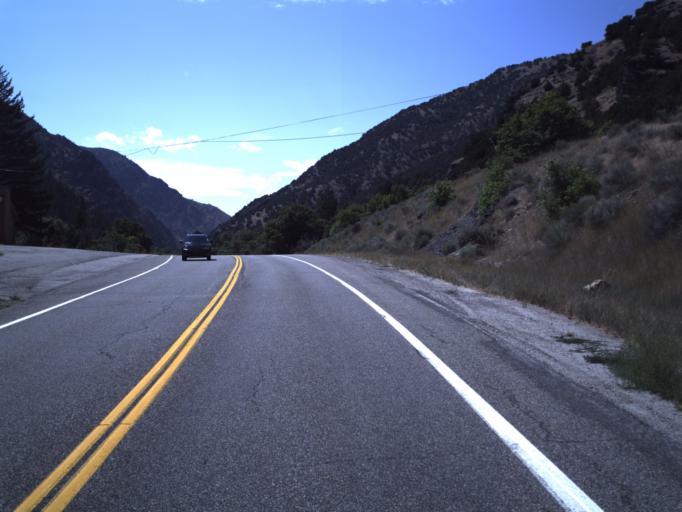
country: US
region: Utah
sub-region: Cache County
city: North Logan
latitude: 41.7484
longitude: -111.7362
